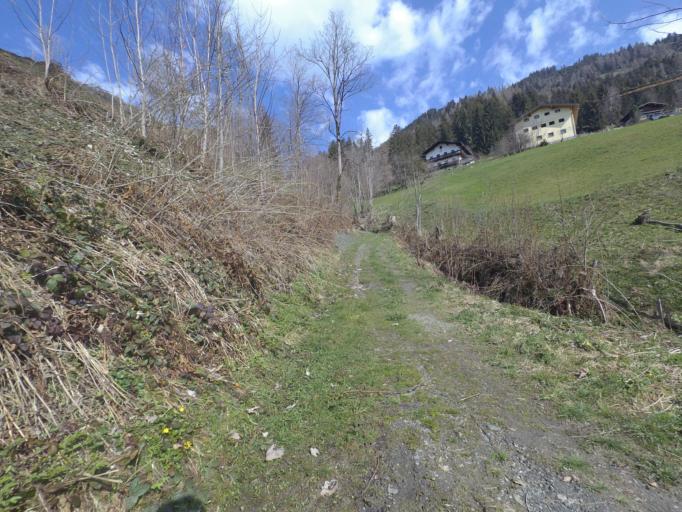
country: AT
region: Salzburg
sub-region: Politischer Bezirk Sankt Johann im Pongau
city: Sankt Veit im Pongau
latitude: 47.3368
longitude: 13.1375
